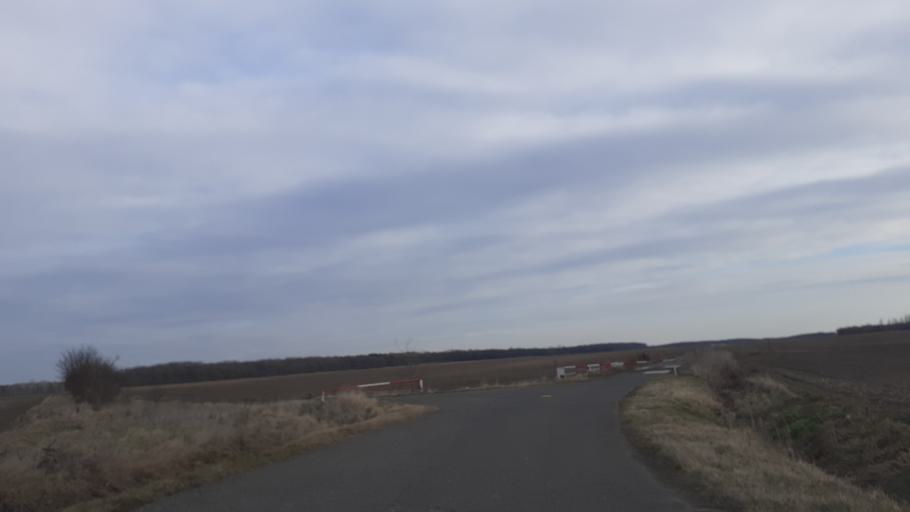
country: HU
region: Fejer
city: Szabadbattyan
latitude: 47.1046
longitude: 18.4434
